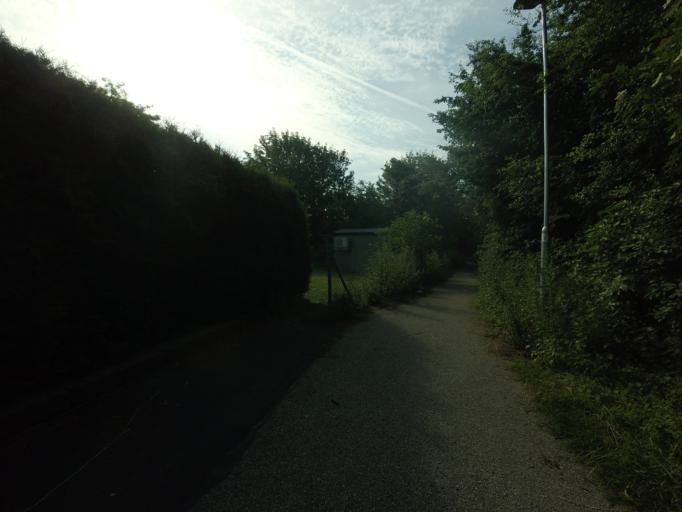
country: SE
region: Skane
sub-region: Malmo
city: Tygelsjo
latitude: 55.4961
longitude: 13.0096
